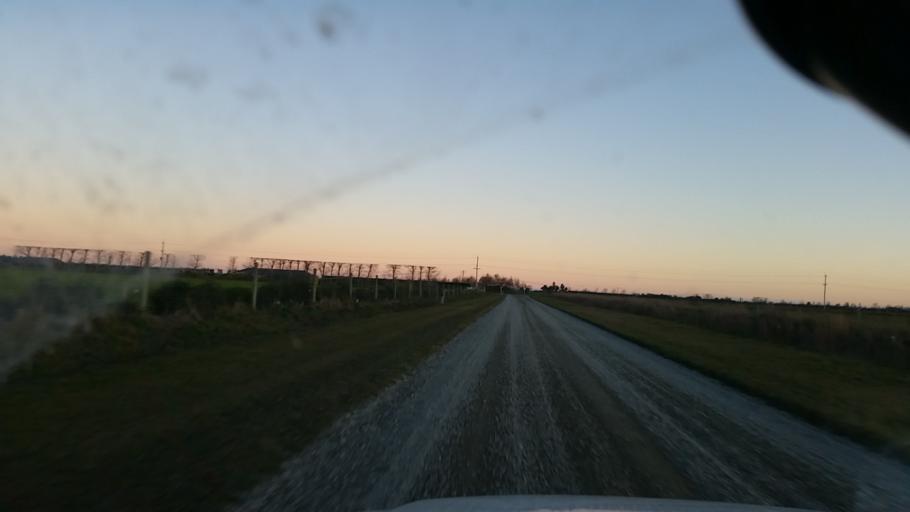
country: NZ
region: Canterbury
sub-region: Ashburton District
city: Tinwald
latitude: -44.0664
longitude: 171.6602
